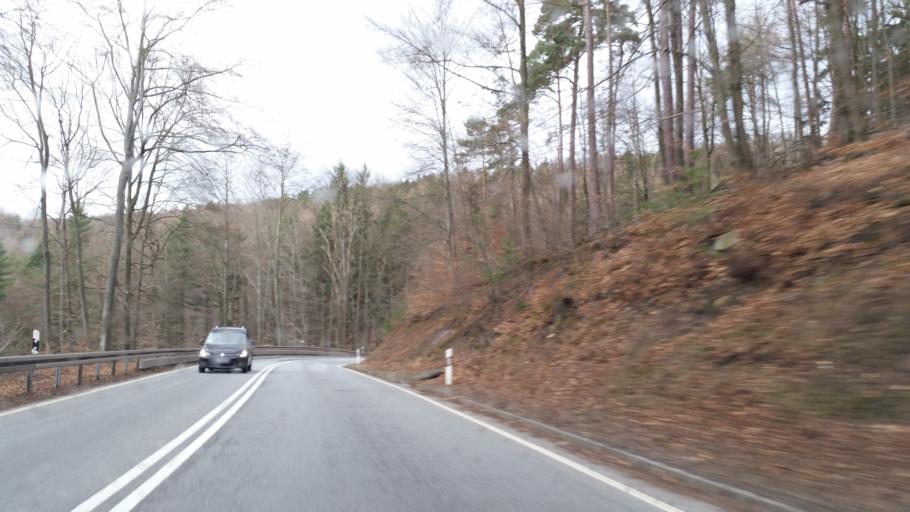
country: DE
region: Bavaria
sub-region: Regierungsbezirk Unterfranken
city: Heigenbrucken
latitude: 49.9977
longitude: 9.3511
